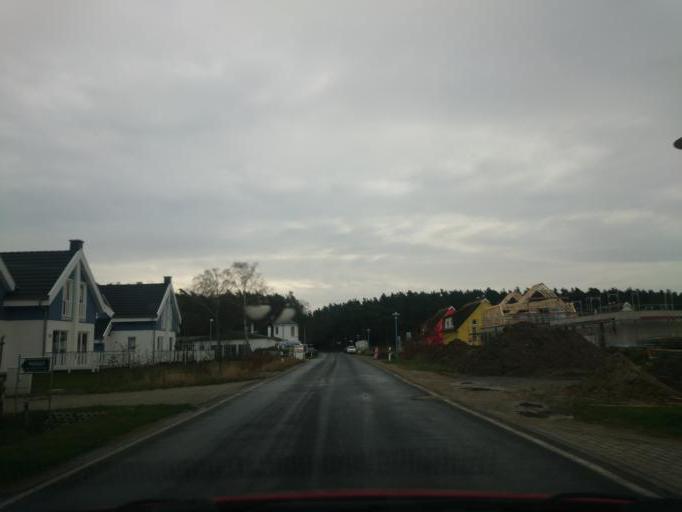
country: DE
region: Mecklenburg-Vorpommern
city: Altenkirchen
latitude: 54.6157
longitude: 13.3735
